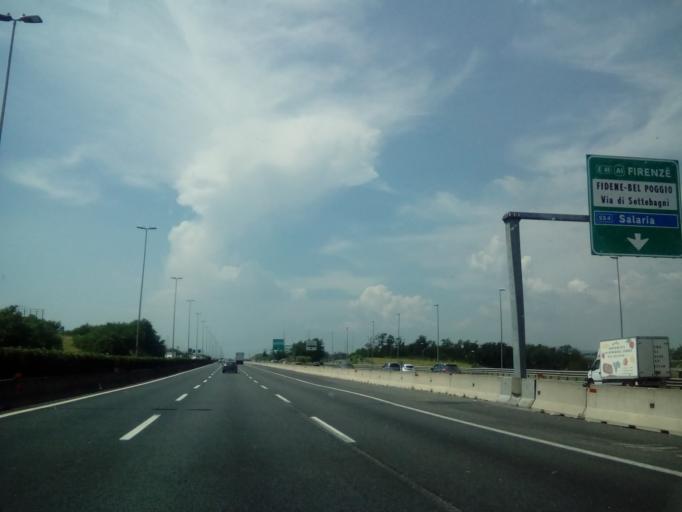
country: IT
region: Latium
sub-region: Citta metropolitana di Roma Capitale
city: Colle Verde
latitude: 41.9756
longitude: 12.5429
